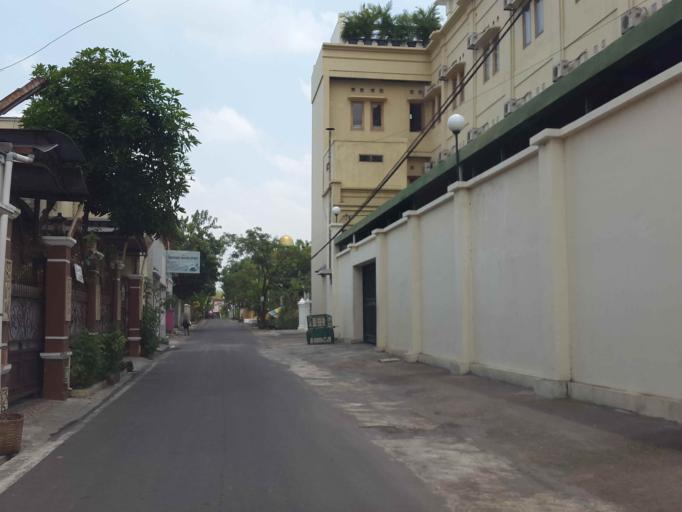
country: ID
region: Central Java
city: Jaten
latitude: -7.5920
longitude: 110.9360
